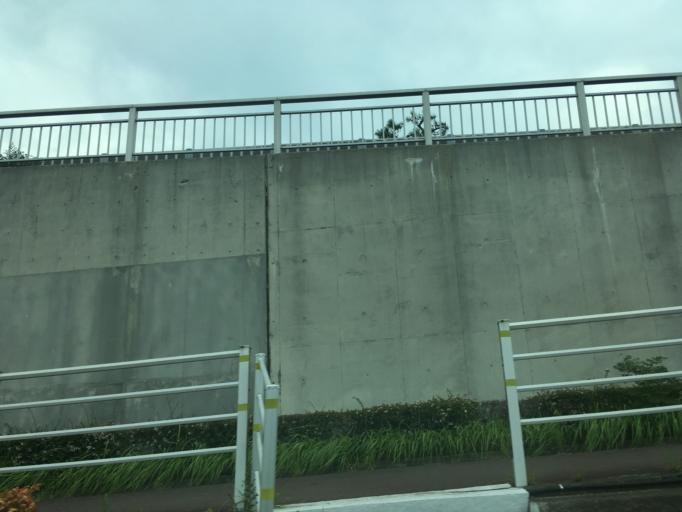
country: JP
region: Hyogo
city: Ashiya
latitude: 34.7175
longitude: 135.3059
